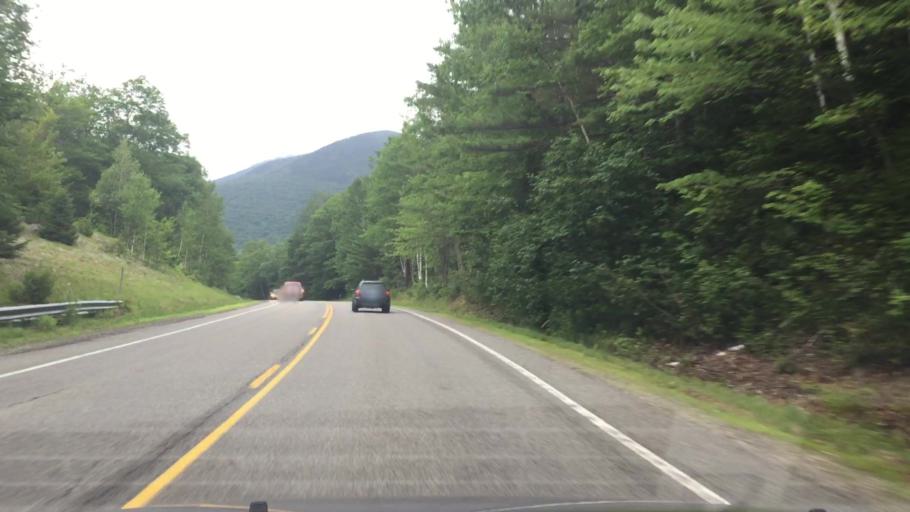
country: US
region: New Hampshire
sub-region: Carroll County
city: North Conway
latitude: 44.0973
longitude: -71.3549
